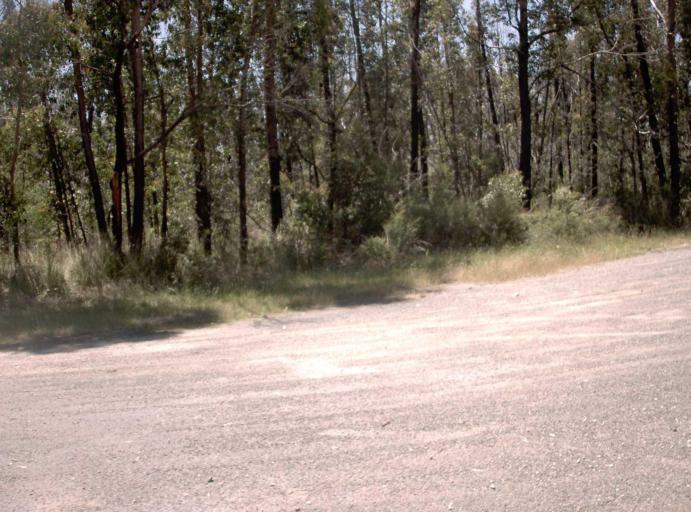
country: AU
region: Victoria
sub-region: East Gippsland
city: Lakes Entrance
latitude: -37.7486
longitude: 148.2257
